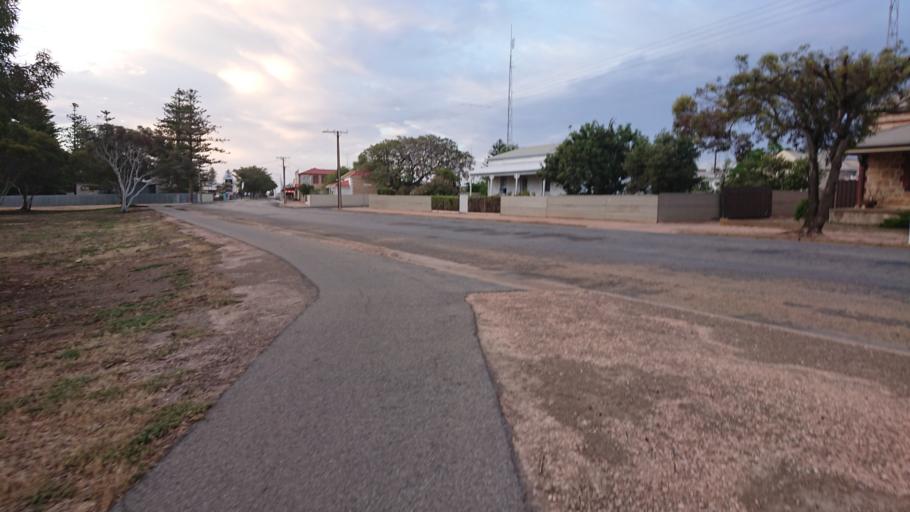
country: AU
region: South Australia
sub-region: Copper Coast
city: Wallaroo
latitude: -33.9335
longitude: 137.6297
